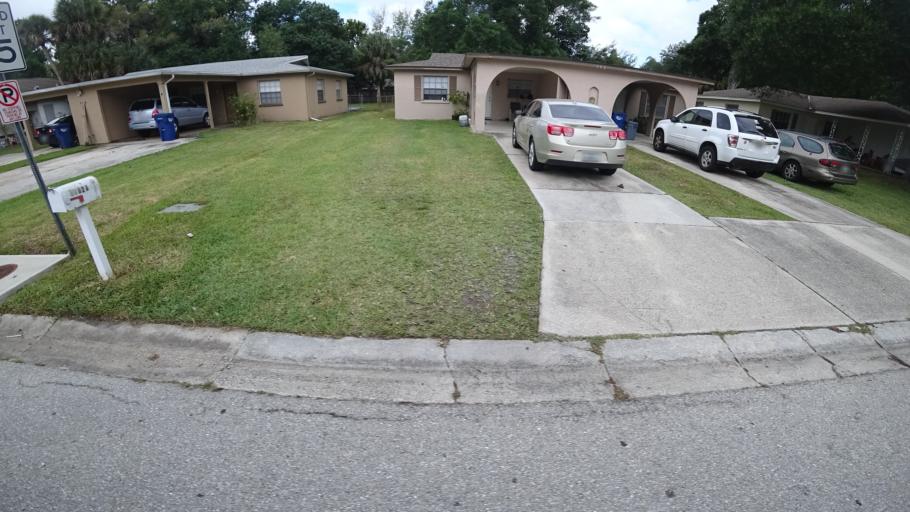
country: US
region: Florida
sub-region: Manatee County
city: South Bradenton
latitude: 27.4533
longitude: -82.5840
